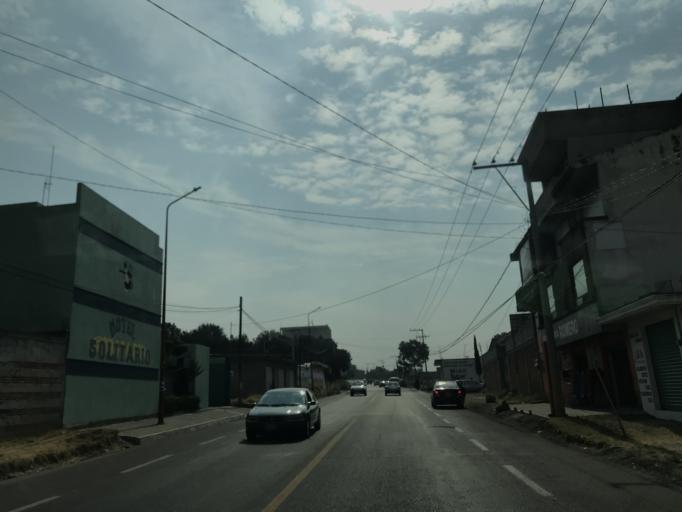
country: MX
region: Tlaxcala
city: Tenancingo
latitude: 19.1514
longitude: -98.2123
